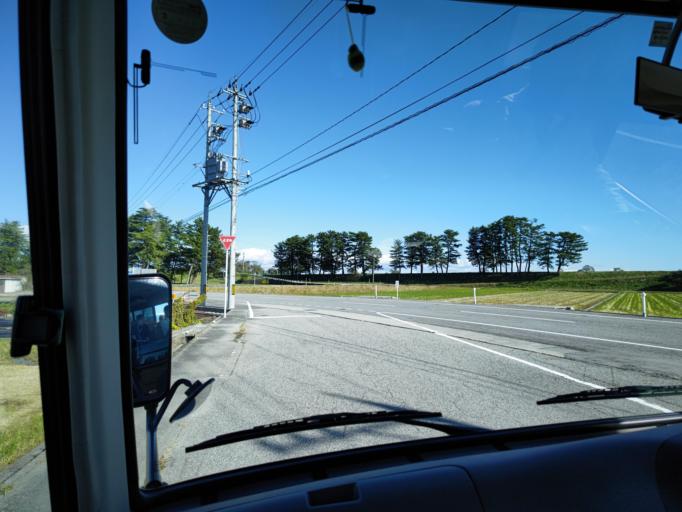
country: JP
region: Toyama
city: Nyuzen
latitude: 36.9062
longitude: 137.4372
